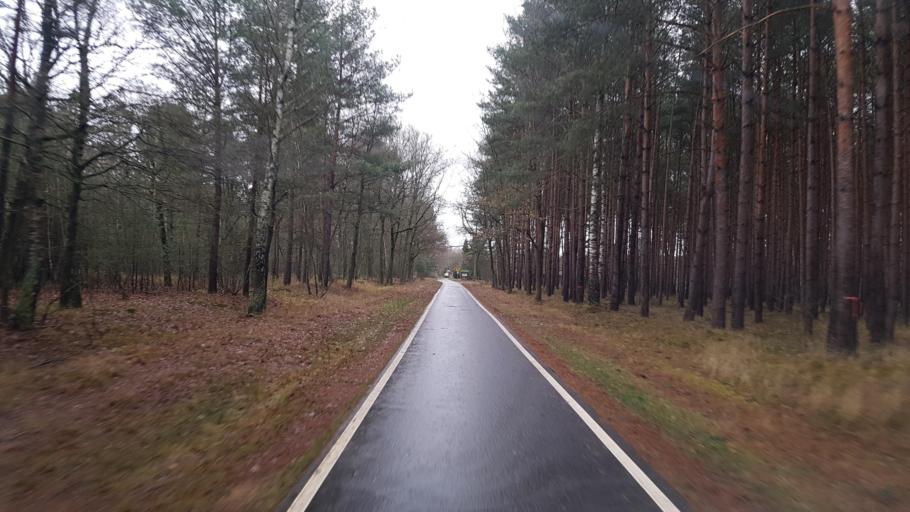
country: DE
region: Brandenburg
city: Tauche
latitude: 52.0911
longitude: 14.1328
